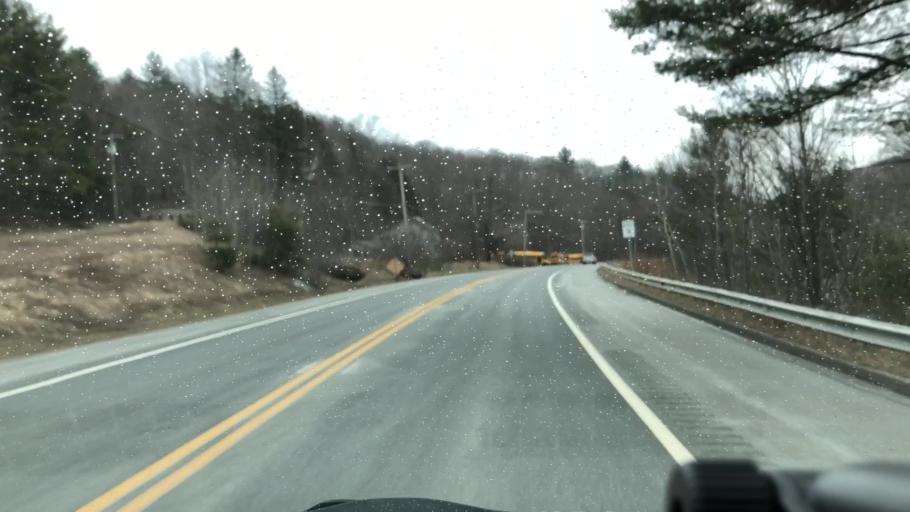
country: US
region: Massachusetts
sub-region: Hampshire County
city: Chesterfield
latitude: 42.4901
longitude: -72.9522
